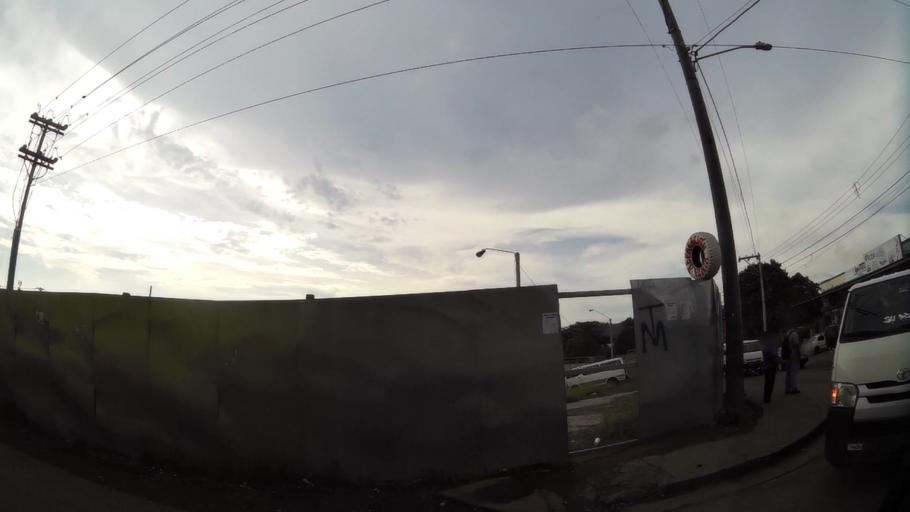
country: PA
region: Panama
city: Tocumen
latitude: 9.1042
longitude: -79.3674
